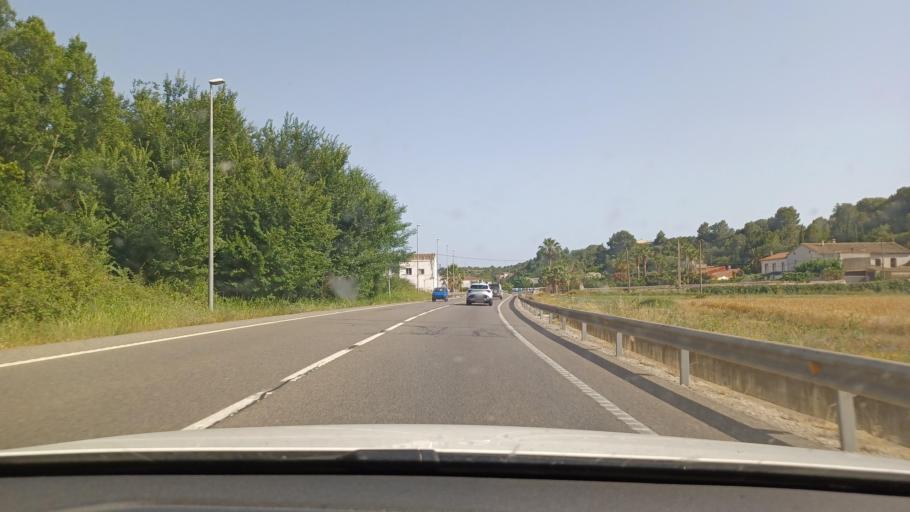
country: ES
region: Catalonia
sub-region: Provincia de Tarragona
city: Tortosa
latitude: 40.7834
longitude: 0.5029
